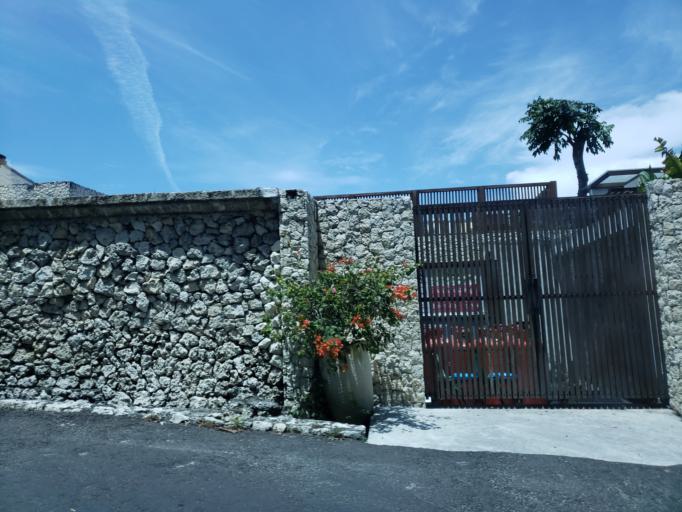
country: ID
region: Bali
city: Jimbaran
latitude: -8.7830
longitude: 115.1616
